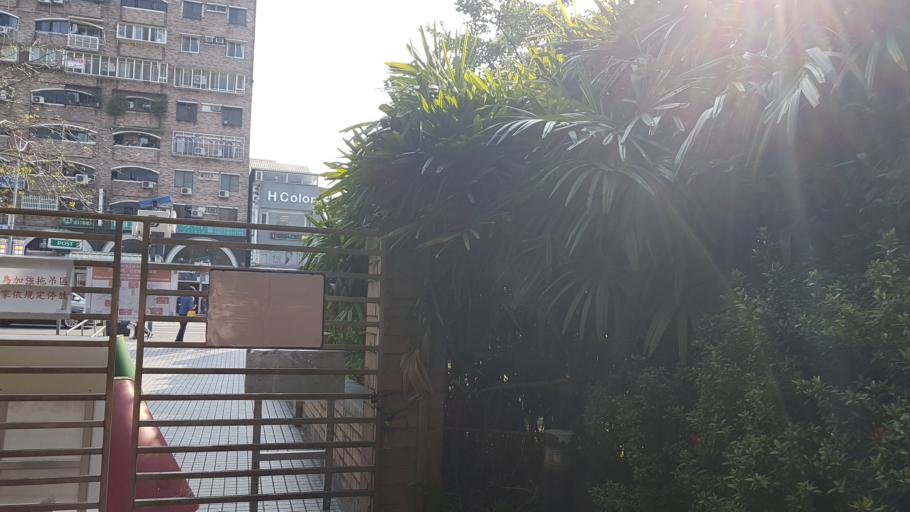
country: TW
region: Taipei
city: Taipei
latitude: 25.0155
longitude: 121.5342
